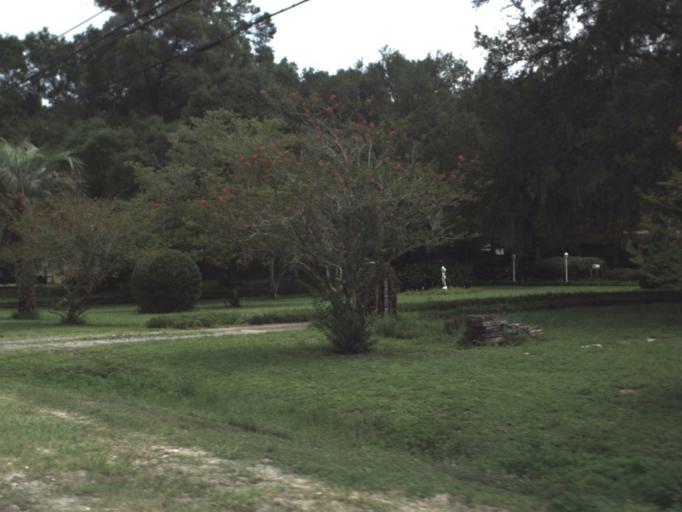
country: US
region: Florida
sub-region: Bay County
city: Hiland Park
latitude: 30.2333
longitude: -85.6030
